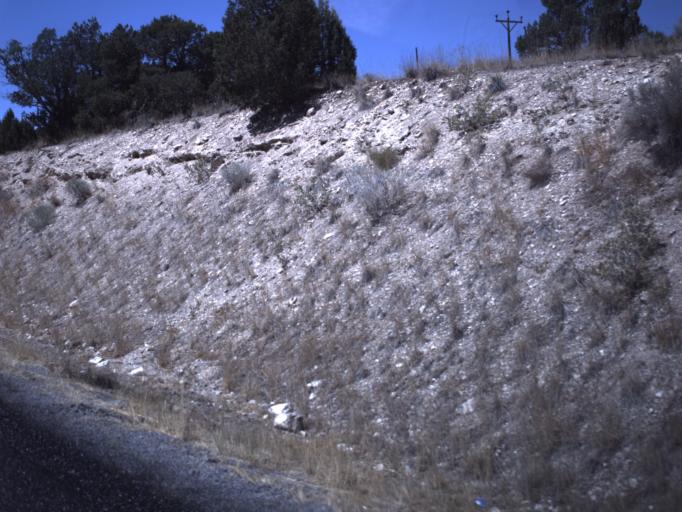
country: US
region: Utah
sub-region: Juab County
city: Nephi
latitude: 39.6994
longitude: -111.9359
